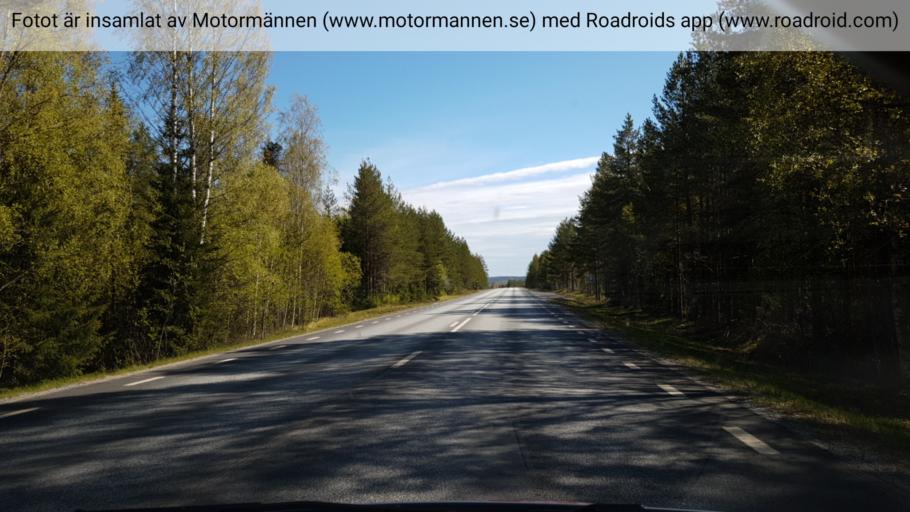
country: SE
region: Vaesterbotten
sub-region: Vannas Kommun
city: Vannasby
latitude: 64.0371
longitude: 20.0101
